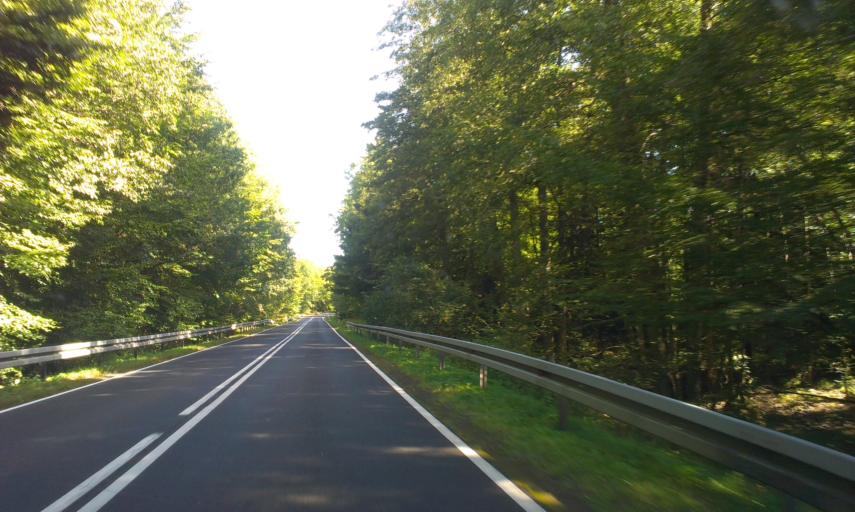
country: PL
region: West Pomeranian Voivodeship
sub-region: Powiat drawski
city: Czaplinek
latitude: 53.5886
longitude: 16.2956
